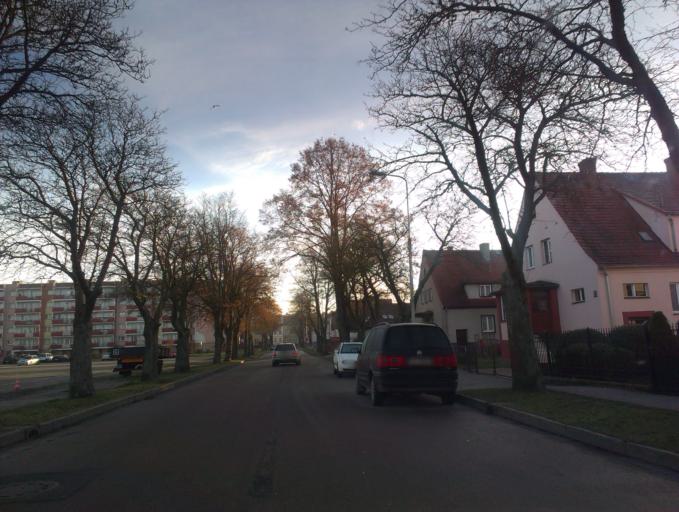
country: PL
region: West Pomeranian Voivodeship
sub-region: Powiat szczecinecki
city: Szczecinek
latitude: 53.7038
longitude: 16.6952
